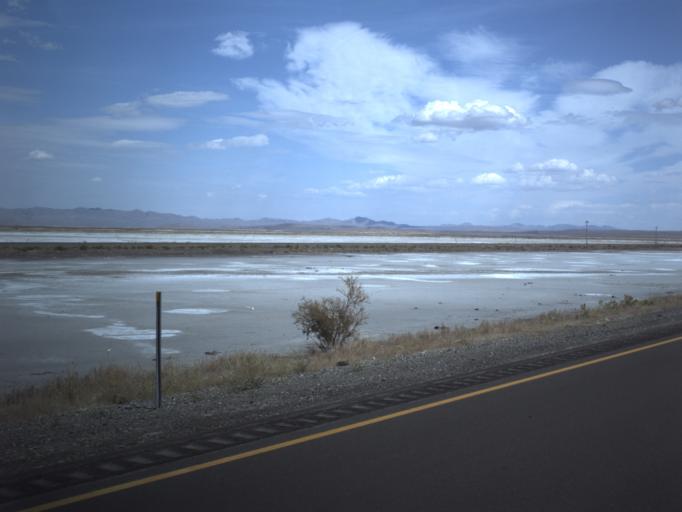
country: US
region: Utah
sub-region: Tooele County
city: Wendover
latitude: 40.7269
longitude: -113.2889
